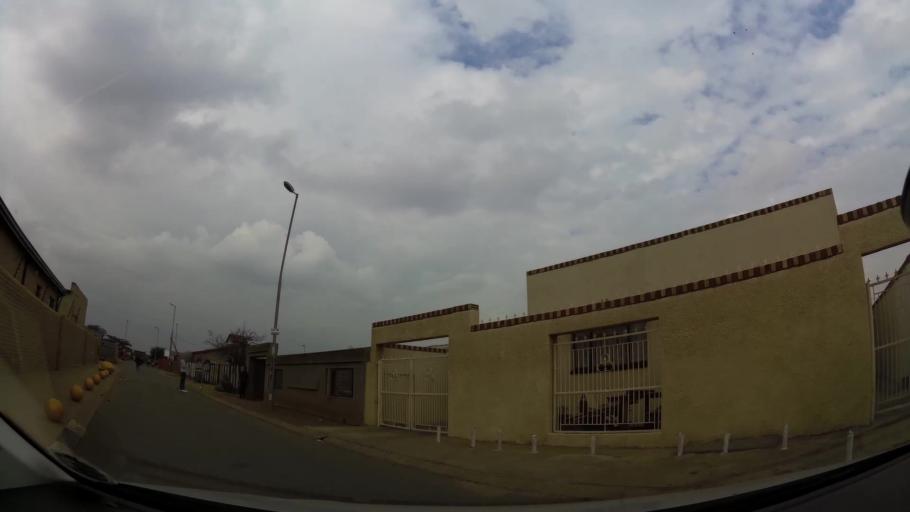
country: ZA
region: Gauteng
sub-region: City of Johannesburg Metropolitan Municipality
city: Soweto
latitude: -26.2621
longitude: 27.8559
